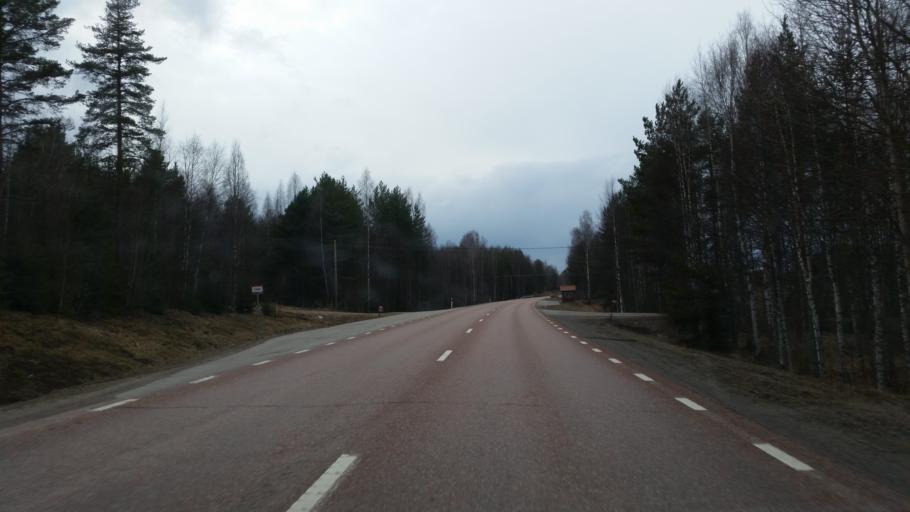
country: SE
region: Gaevleborg
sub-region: Ljusdals Kommun
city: Ljusdal
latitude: 61.8071
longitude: 16.1004
